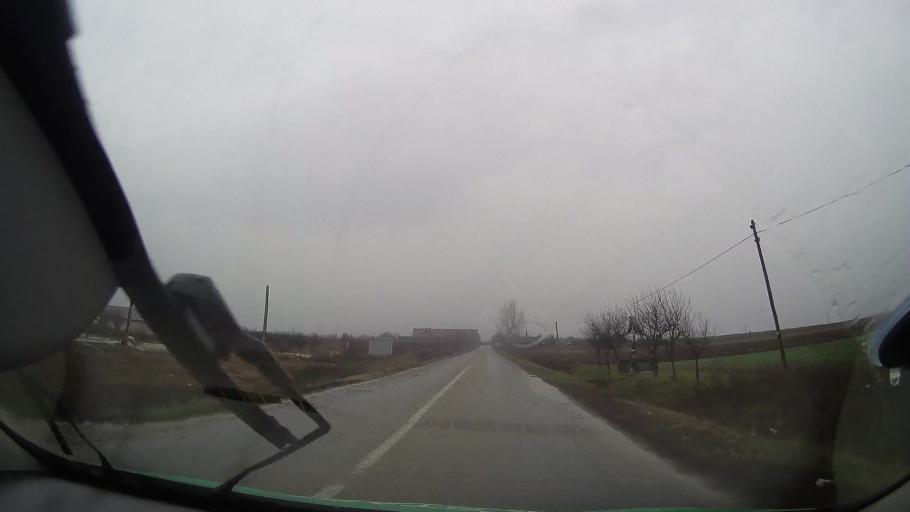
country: RO
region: Bihor
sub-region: Comuna Tulca
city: Tulca
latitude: 46.7856
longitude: 21.7918
